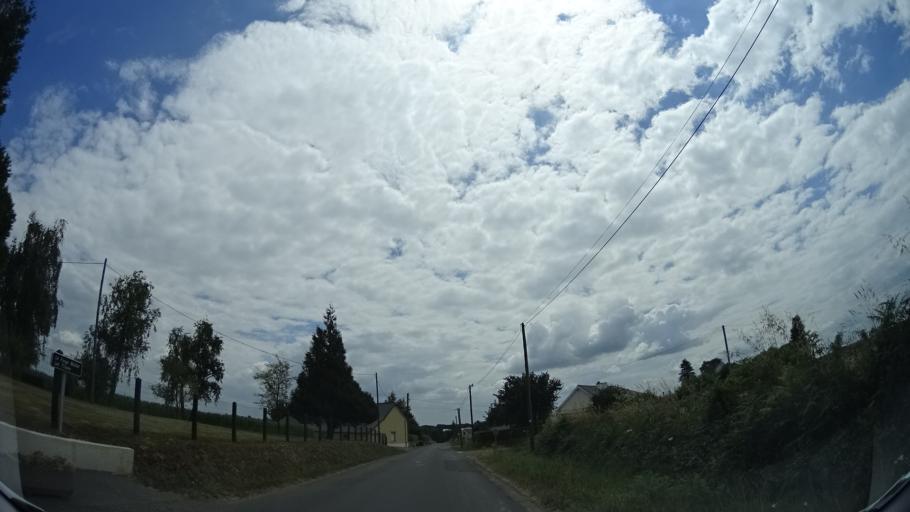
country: FR
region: Brittany
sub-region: Departement d'Ille-et-Vilaine
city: La Chapelle-des-Fougeretz
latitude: 48.1743
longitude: -1.7533
